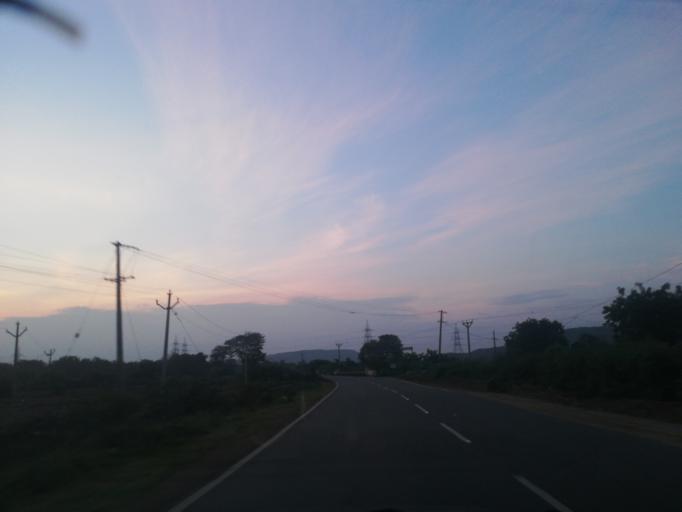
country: IN
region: Andhra Pradesh
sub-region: Guntur
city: Macherla
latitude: 16.6763
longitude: 79.2660
